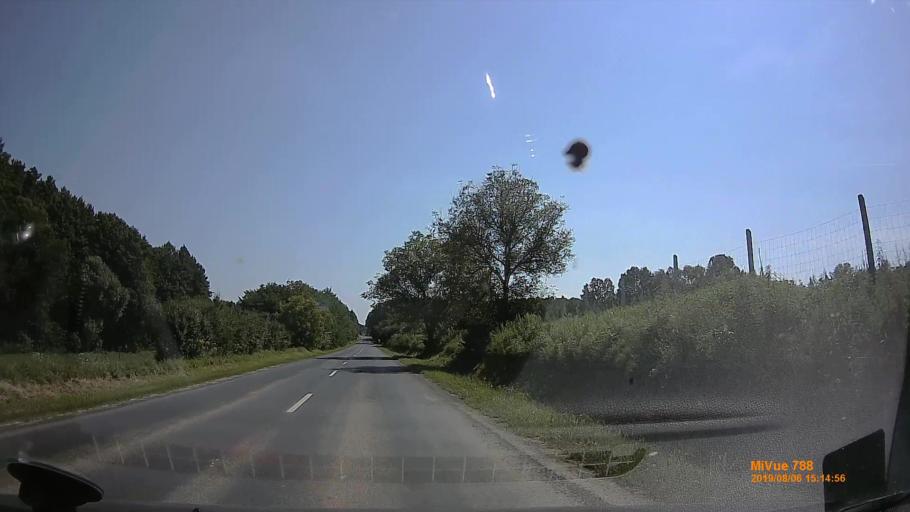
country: HU
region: Zala
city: Murakeresztur
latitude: 46.3342
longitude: 16.9716
